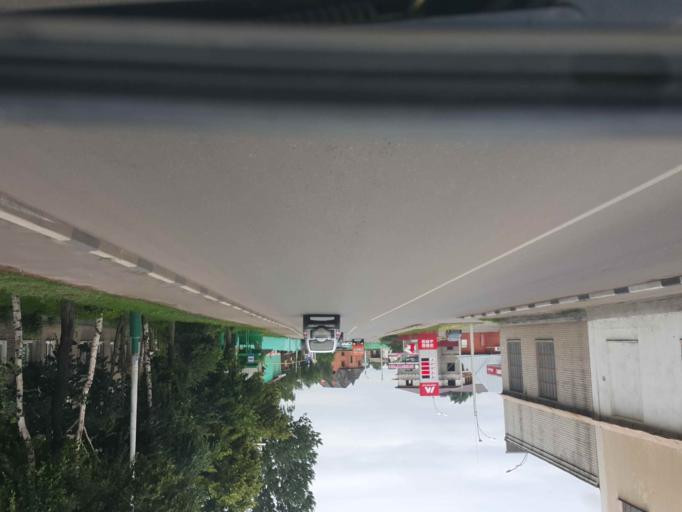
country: RU
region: Tambov
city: Zavoronezhskoye
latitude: 52.8821
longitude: 40.5269
